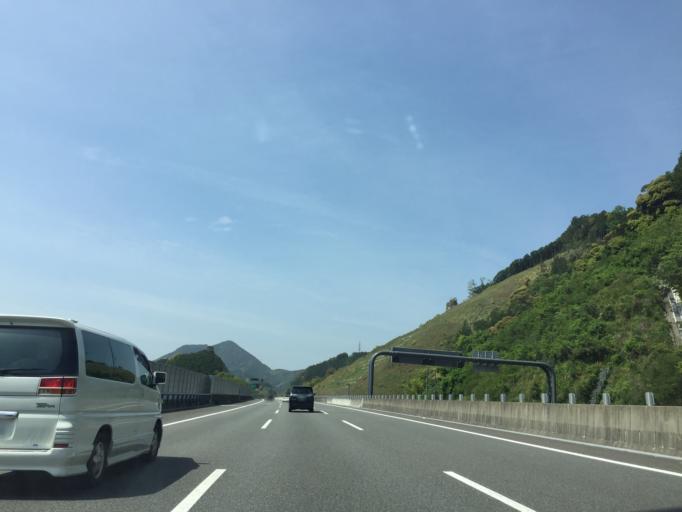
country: JP
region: Shizuoka
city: Shizuoka-shi
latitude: 35.0343
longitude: 138.3639
